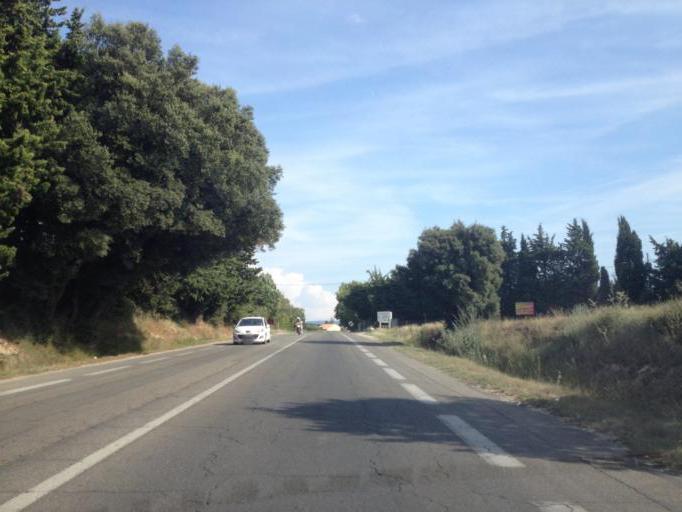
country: FR
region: Provence-Alpes-Cote d'Azur
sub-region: Departement du Vaucluse
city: Aubignan
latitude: 44.0814
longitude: 5.0378
